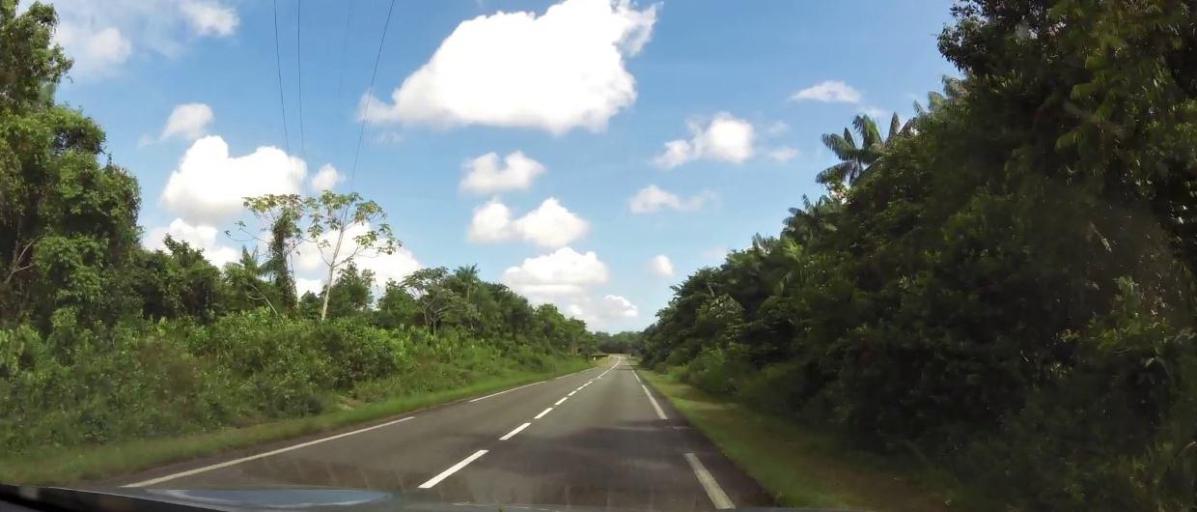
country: GF
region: Guyane
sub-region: Guyane
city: Sinnamary
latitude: 5.3707
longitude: -52.9646
